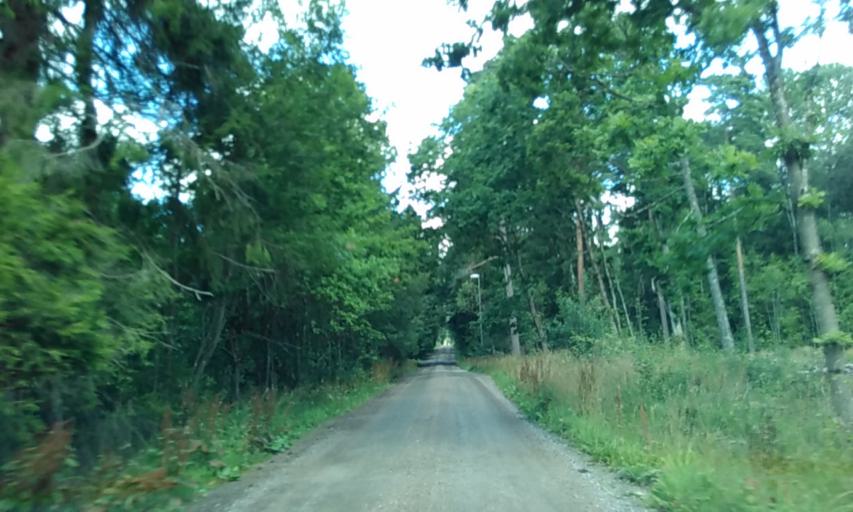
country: SE
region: Vaestra Goetaland
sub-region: Lerums Kommun
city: Grabo
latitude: 57.9104
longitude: 12.3740
